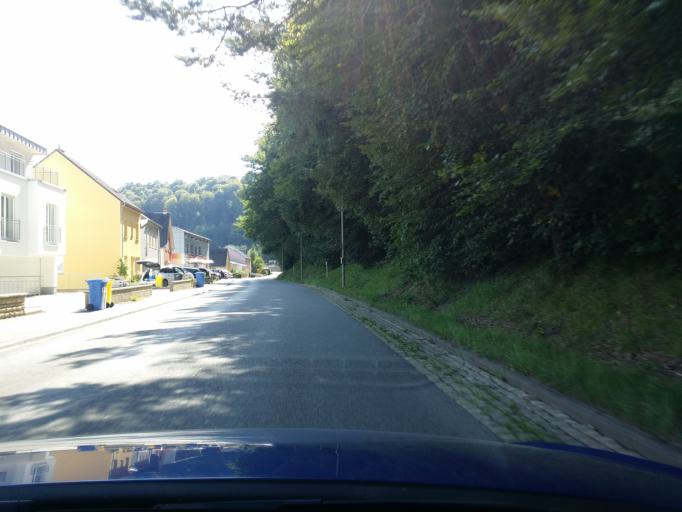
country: LU
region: Luxembourg
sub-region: Canton de Capellen
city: Kopstal
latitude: 49.6716
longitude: 6.0770
